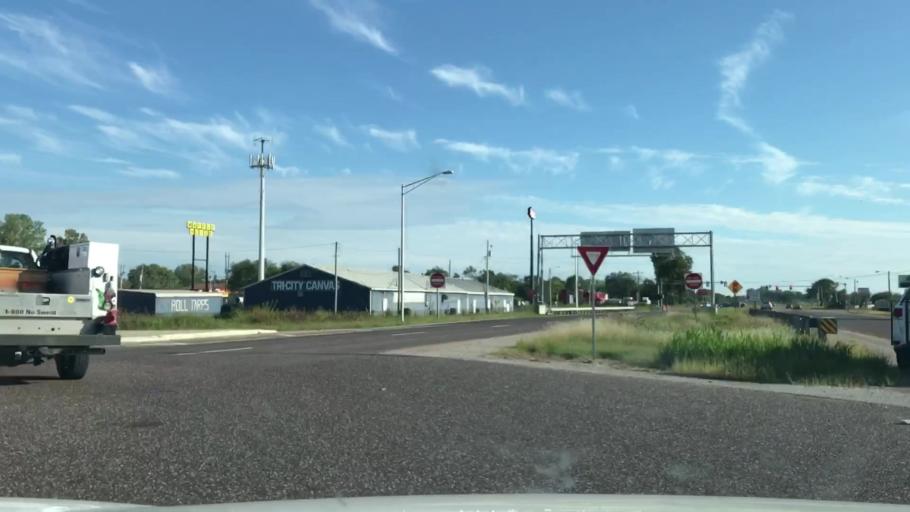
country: US
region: Illinois
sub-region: Madison County
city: Mitchell
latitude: 38.7643
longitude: -90.1244
